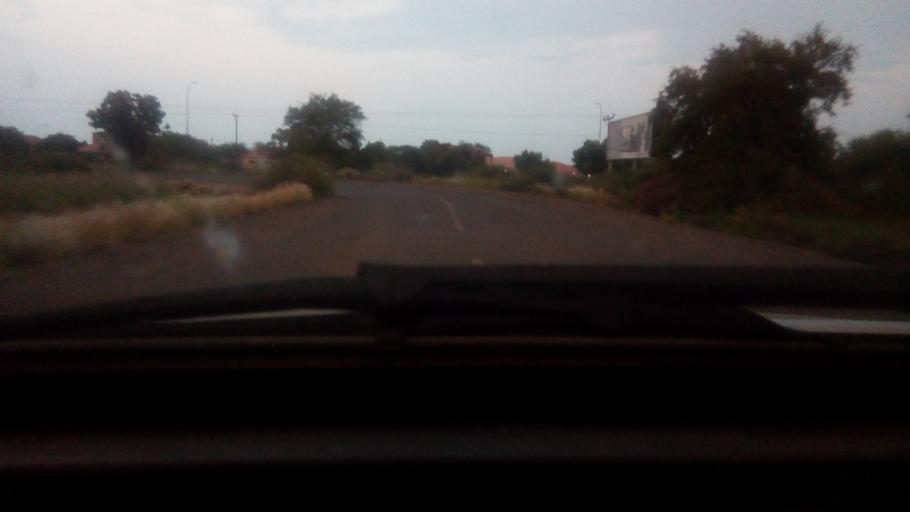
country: BW
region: Kweneng
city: Mmopone
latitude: -24.5904
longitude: 25.9169
